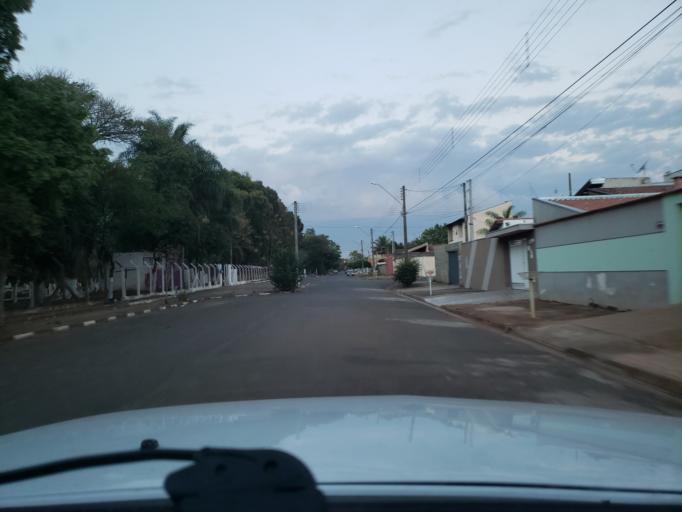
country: BR
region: Sao Paulo
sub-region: Moji-Guacu
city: Mogi-Gaucu
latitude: -22.3421
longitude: -46.9324
